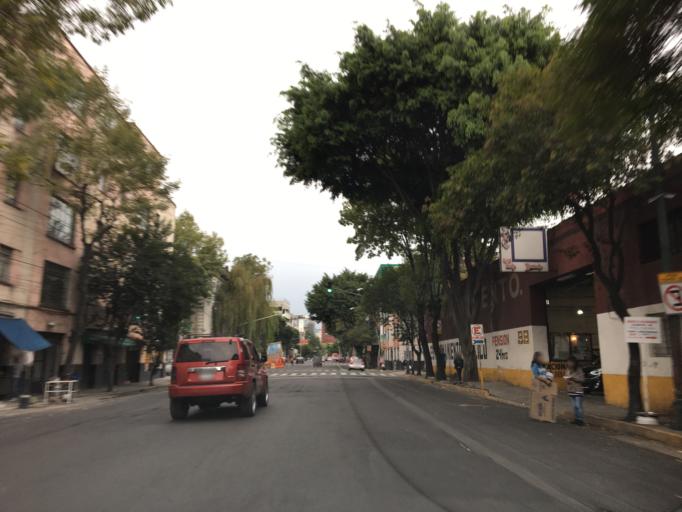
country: MX
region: Mexico City
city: Cuauhtemoc
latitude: 19.4348
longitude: -99.1610
